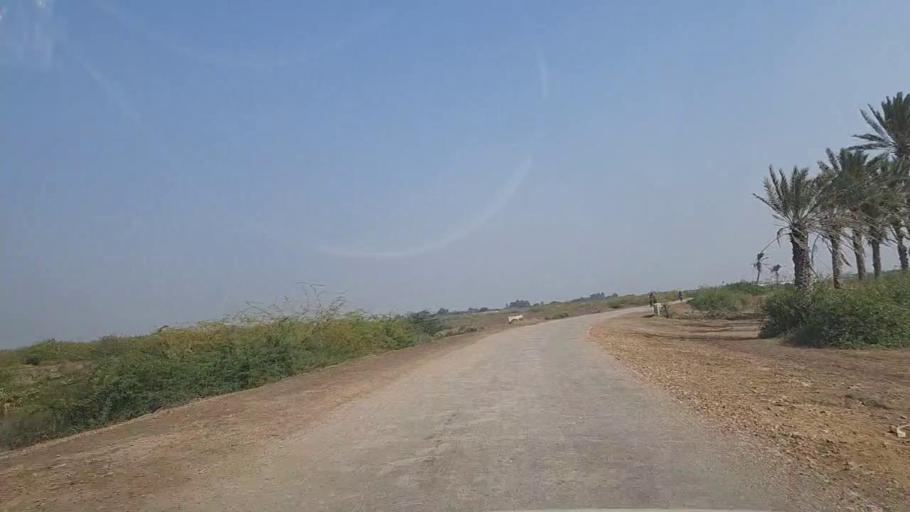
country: PK
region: Sindh
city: Keti Bandar
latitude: 24.2492
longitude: 67.7133
